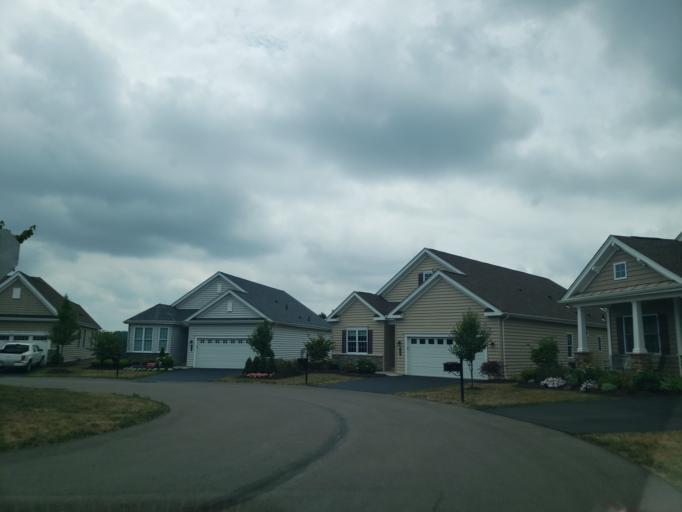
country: US
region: Pennsylvania
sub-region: Allegheny County
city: Emsworth
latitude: 40.5351
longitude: -80.1198
